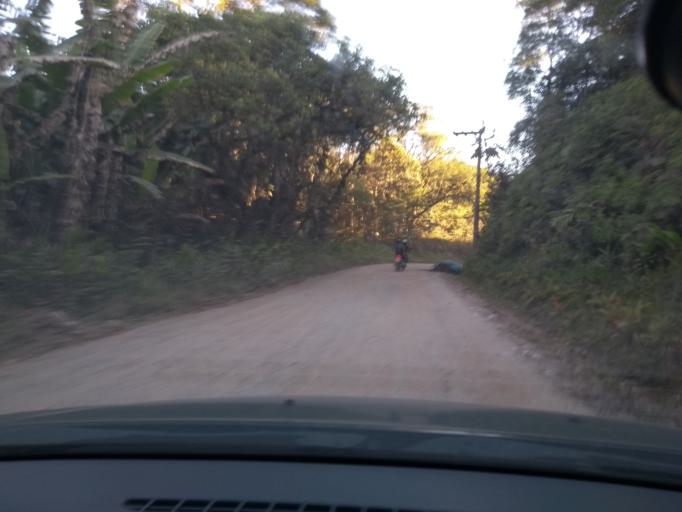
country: BR
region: Sao Paulo
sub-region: Sao Bernardo Do Campo
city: Sao Bernardo do Campo
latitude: -23.7742
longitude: -46.5012
